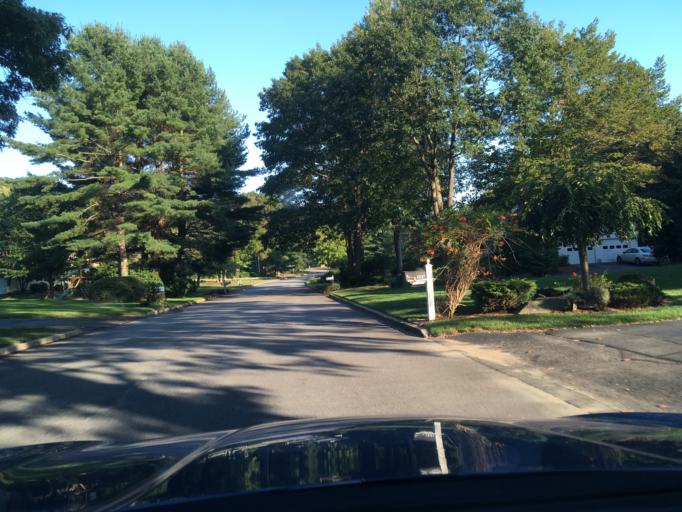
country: US
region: Rhode Island
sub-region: Kent County
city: West Warwick
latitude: 41.6501
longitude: -71.5074
